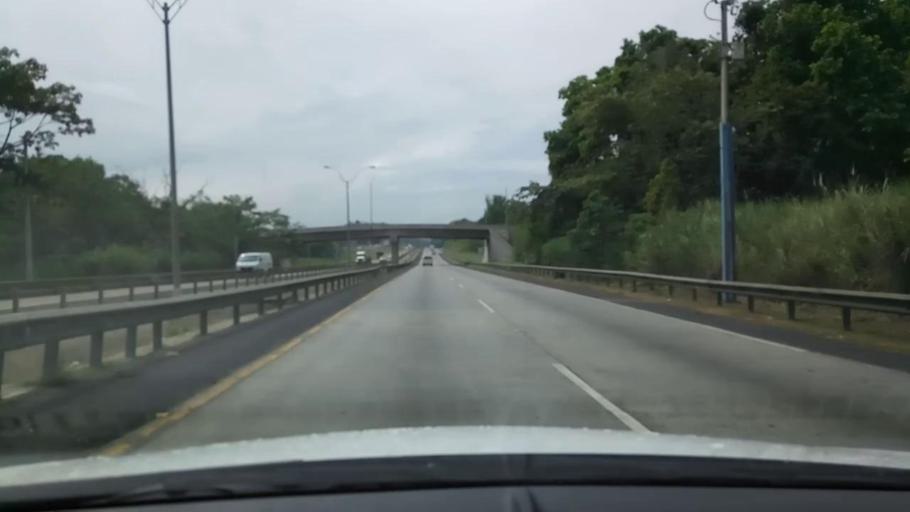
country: PA
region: Panama
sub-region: Distrito de Panama
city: Paraiso
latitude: 9.0360
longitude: -79.5765
